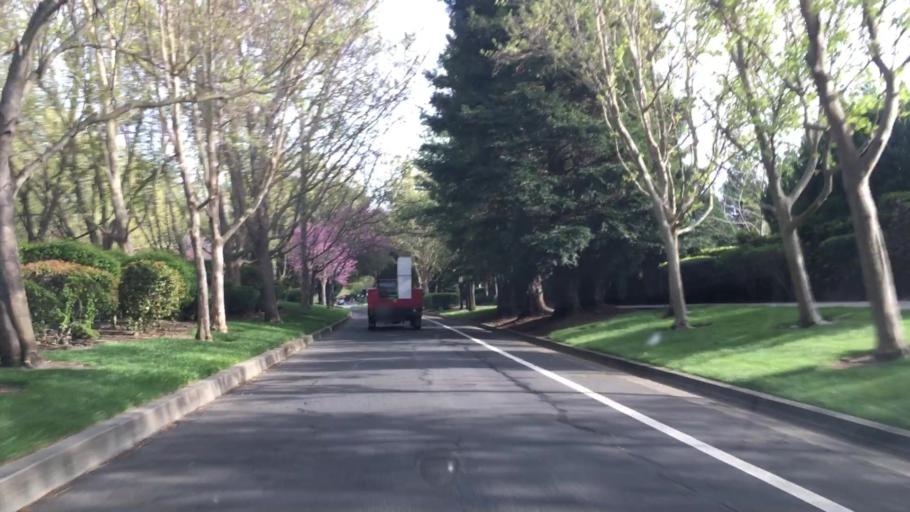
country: US
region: California
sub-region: Solano County
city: Green Valley
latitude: 38.2281
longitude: -122.1483
